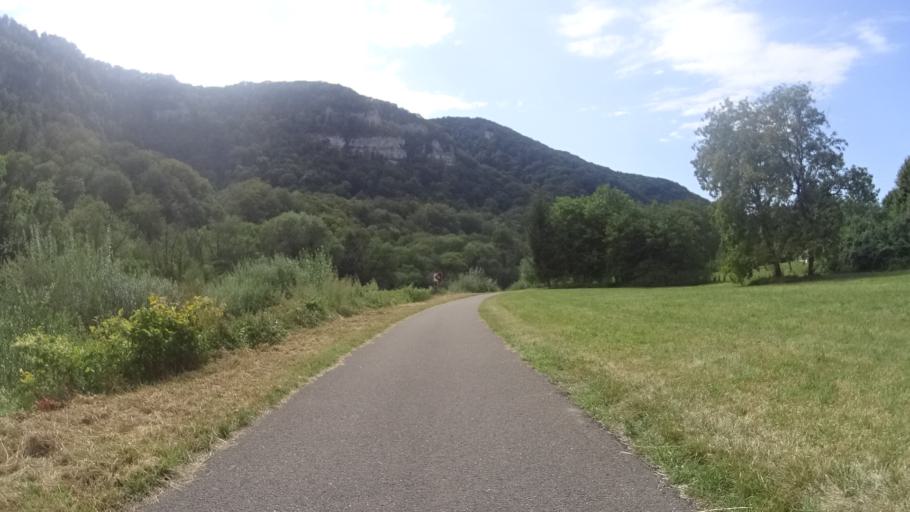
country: FR
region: Franche-Comte
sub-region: Departement du Doubs
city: Roulans
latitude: 47.2961
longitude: 6.2327
